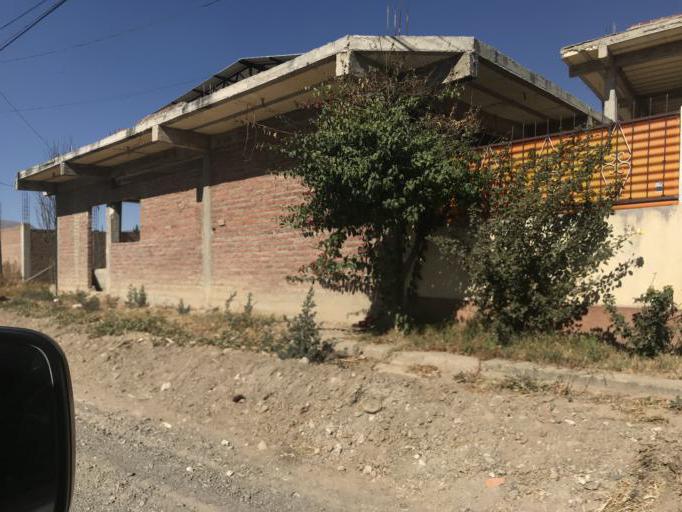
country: BO
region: Cochabamba
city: Punata
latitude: -17.5563
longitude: -65.8605
